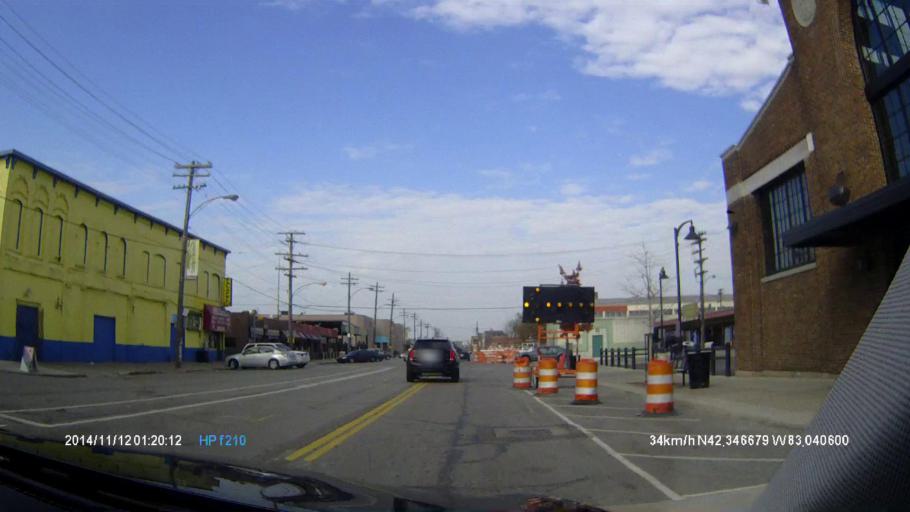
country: US
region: Michigan
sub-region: Wayne County
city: Detroit
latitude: 42.3469
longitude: -83.0408
